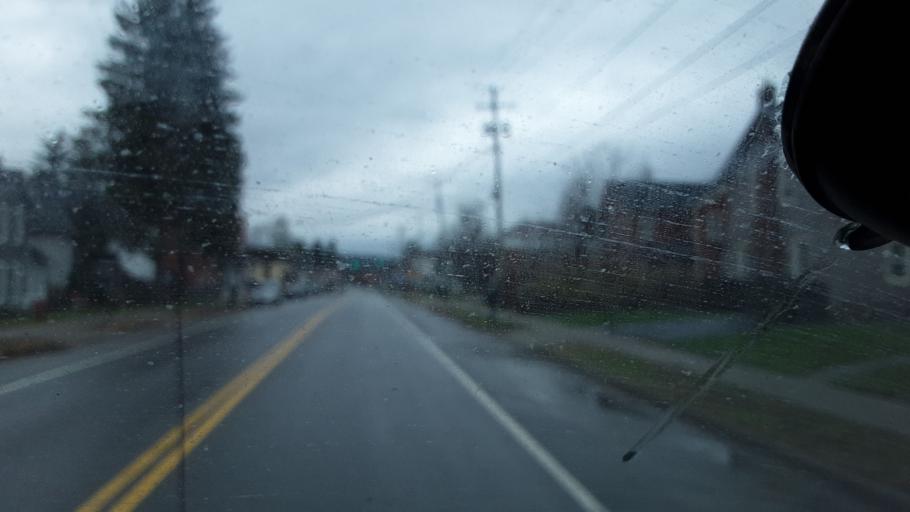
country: US
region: New York
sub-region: Erie County
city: Holland
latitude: 42.6403
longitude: -78.5405
